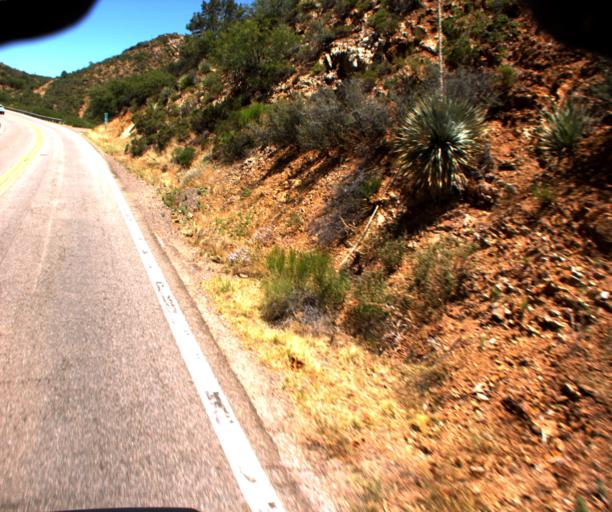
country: US
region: Arizona
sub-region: Pinal County
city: Kearny
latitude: 33.2051
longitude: -110.8021
